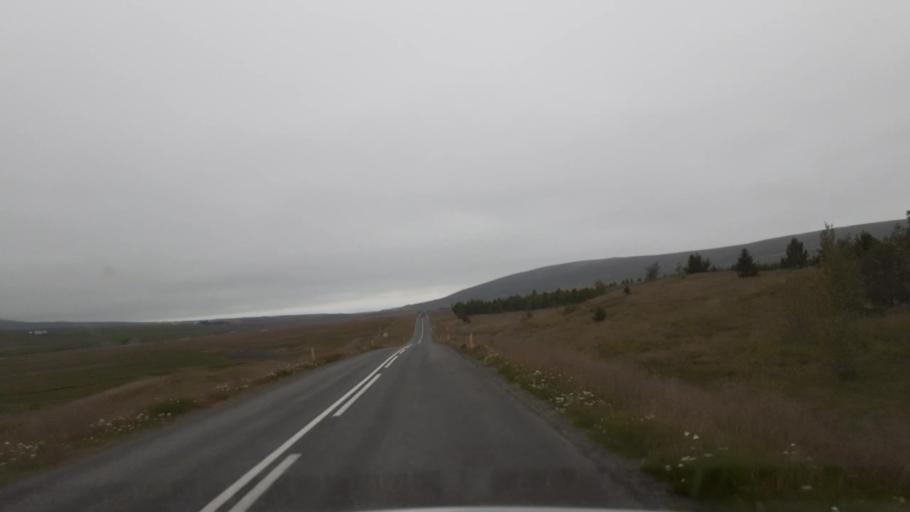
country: IS
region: Northeast
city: Siglufjoerdur
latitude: 65.7370
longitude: -19.1285
